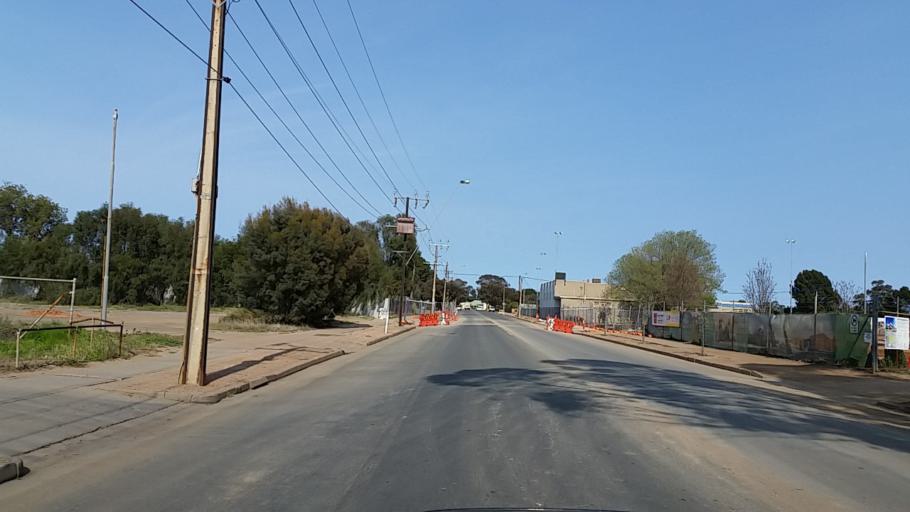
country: AU
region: South Australia
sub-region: Port Pirie City and Dists
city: Port Pirie
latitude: -33.1821
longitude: 138.0079
